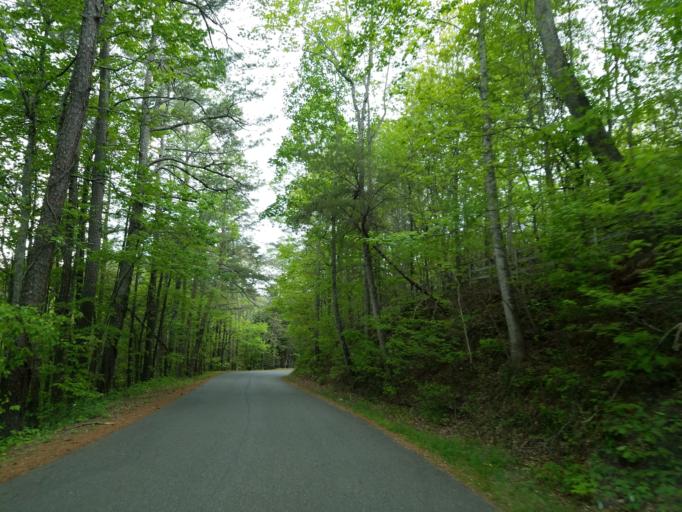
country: US
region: Georgia
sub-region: Pickens County
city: Jasper
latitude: 34.4406
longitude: -84.4836
